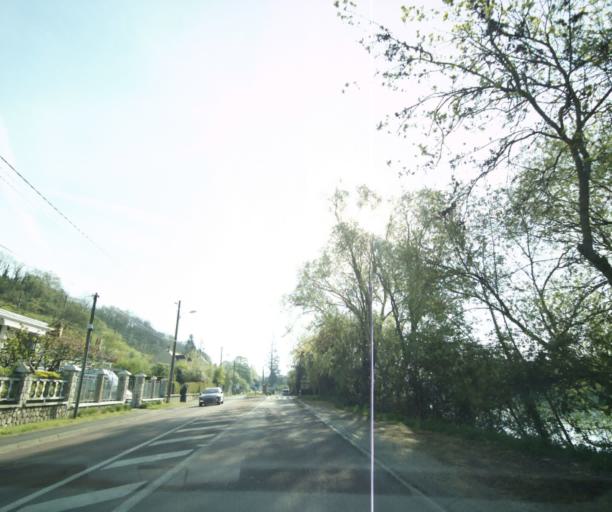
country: FR
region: Ile-de-France
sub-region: Departement de Seine-et-Marne
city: Saint-Mammes
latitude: 48.3936
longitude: 2.8175
